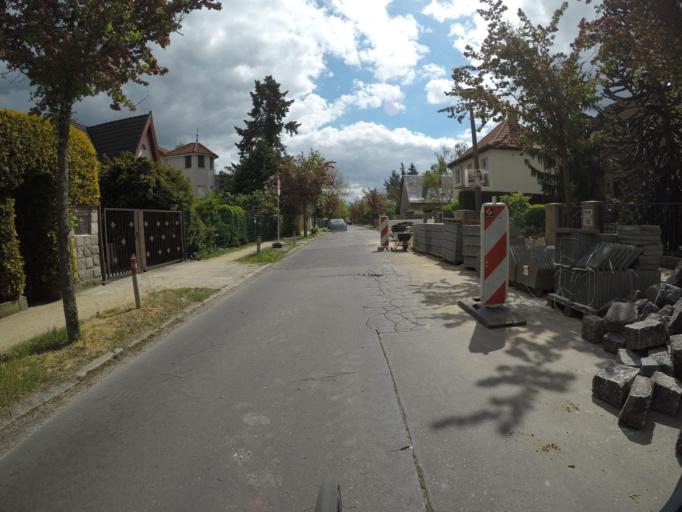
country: DE
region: Berlin
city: Fennpfuhl
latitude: 52.5382
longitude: 13.4544
